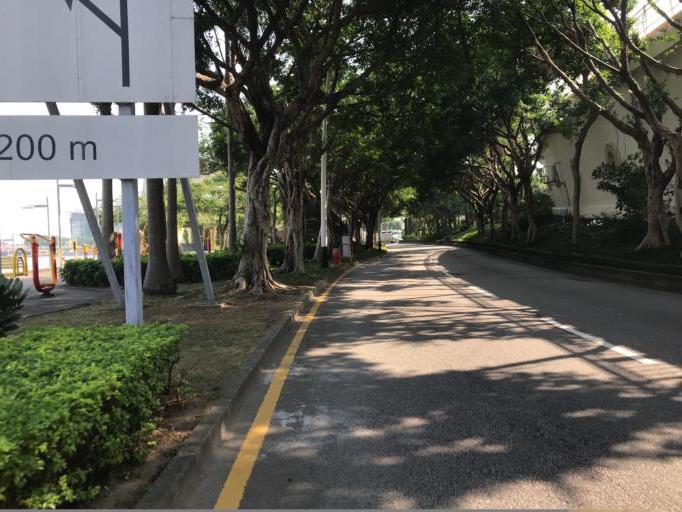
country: CN
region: Guangdong
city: Wanzai
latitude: 22.1806
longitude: 113.5318
